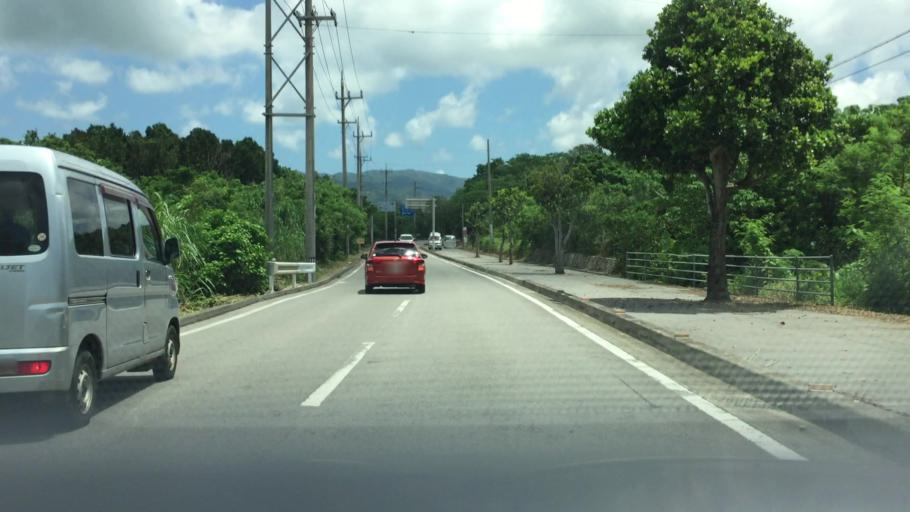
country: JP
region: Okinawa
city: Ishigaki
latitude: 24.3810
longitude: 124.1336
